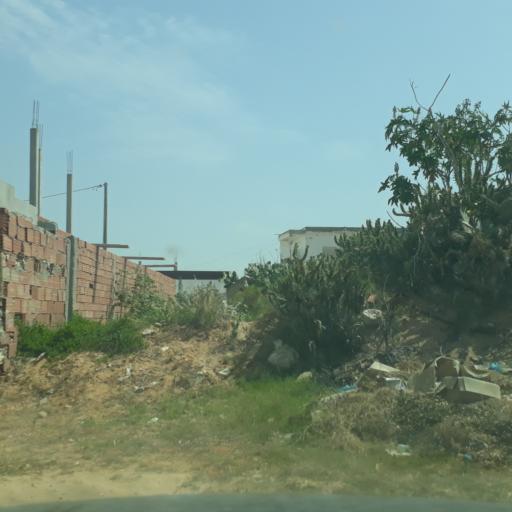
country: TN
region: Safaqis
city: Al Qarmadah
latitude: 34.7977
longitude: 10.7672
